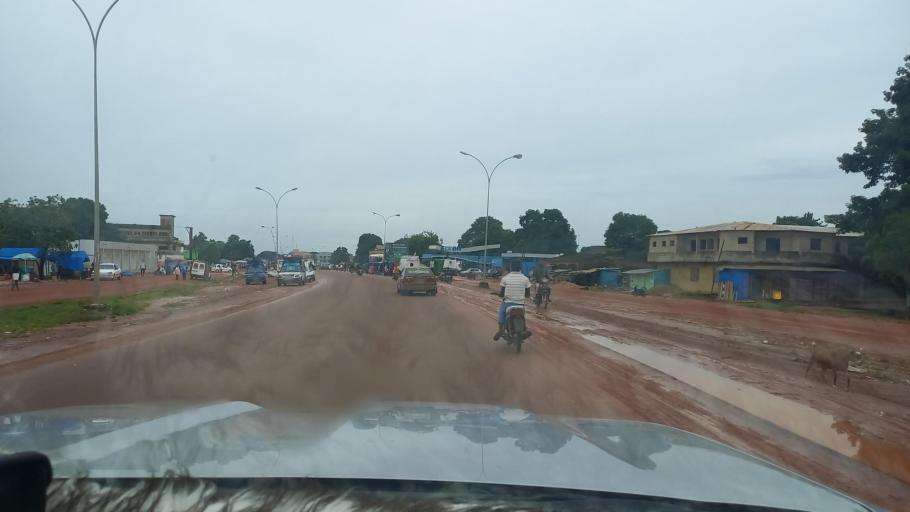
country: SN
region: Ziguinchor
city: Ziguinchor
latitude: 12.5644
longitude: -16.2671
